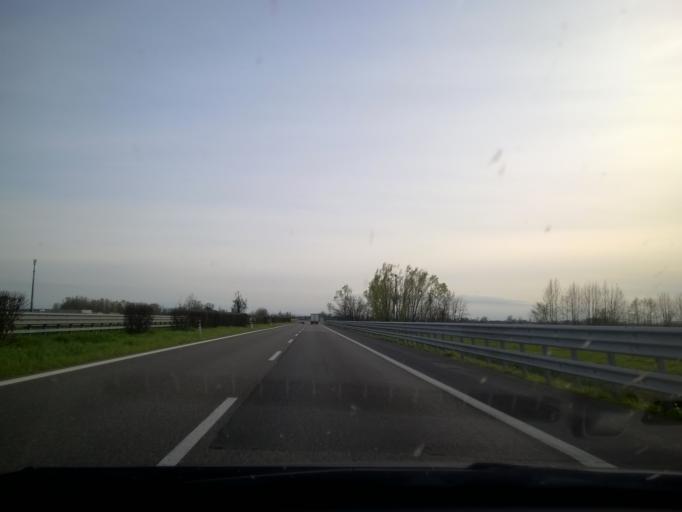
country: IT
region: Lombardy
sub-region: Provincia di Cremona
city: Dosimo
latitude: 45.1809
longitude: 10.0899
